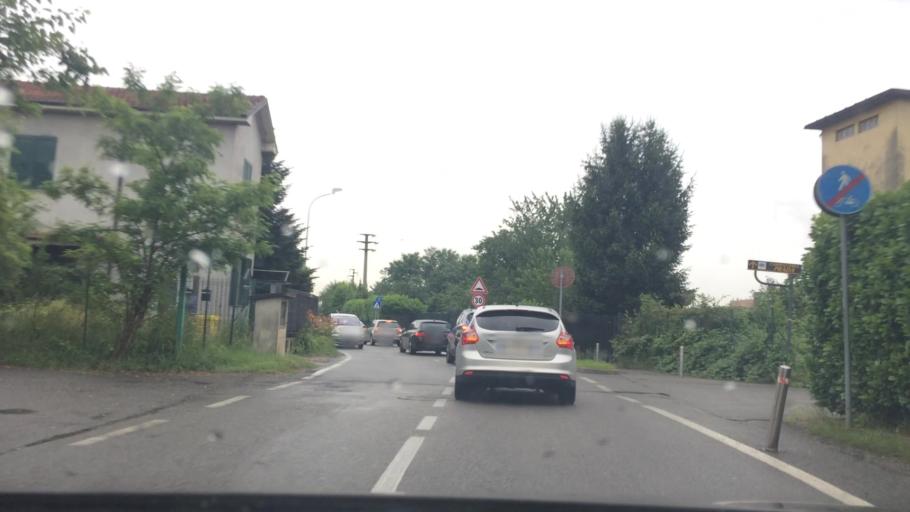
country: IT
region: Lombardy
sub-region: Citta metropolitana di Milano
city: Pero
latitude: 45.5128
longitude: 9.0714
